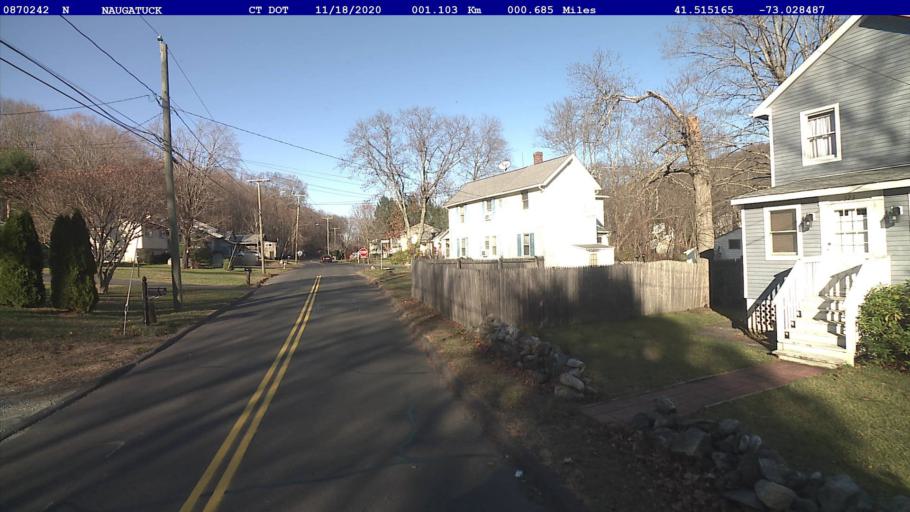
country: US
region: Connecticut
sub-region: New Haven County
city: Naugatuck
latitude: 41.5152
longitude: -73.0285
